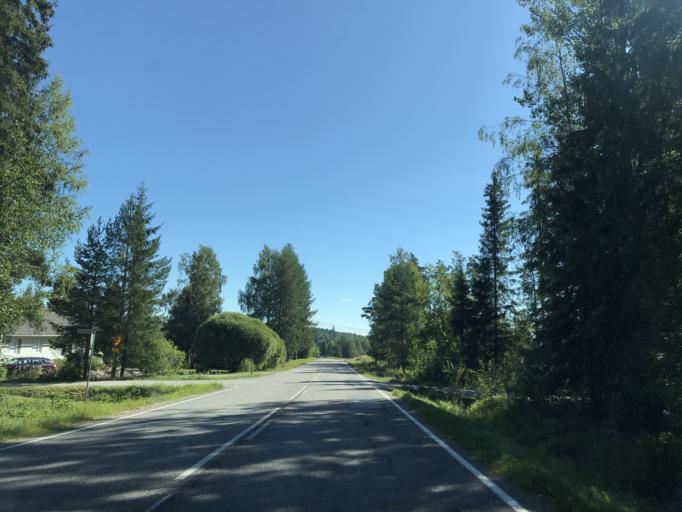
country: FI
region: Paijanne Tavastia
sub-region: Lahti
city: Orimattila
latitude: 60.8100
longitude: 25.6962
